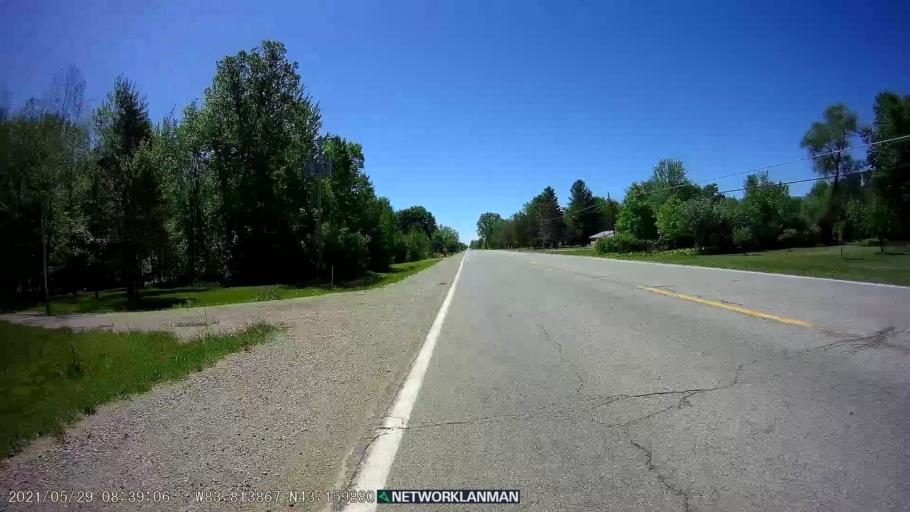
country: US
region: Michigan
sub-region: Genesee County
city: Montrose
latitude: 43.1600
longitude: -83.8139
